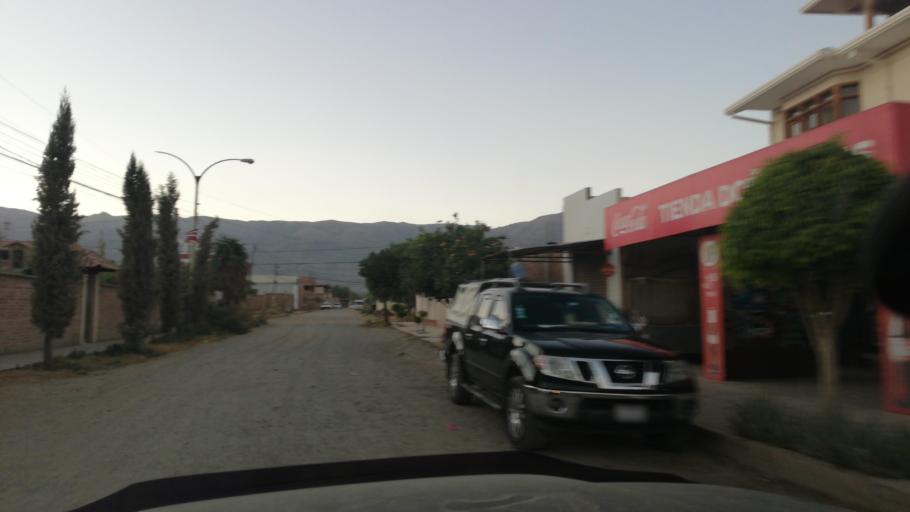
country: BO
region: Cochabamba
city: Cochabamba
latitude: -17.3859
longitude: -66.2189
